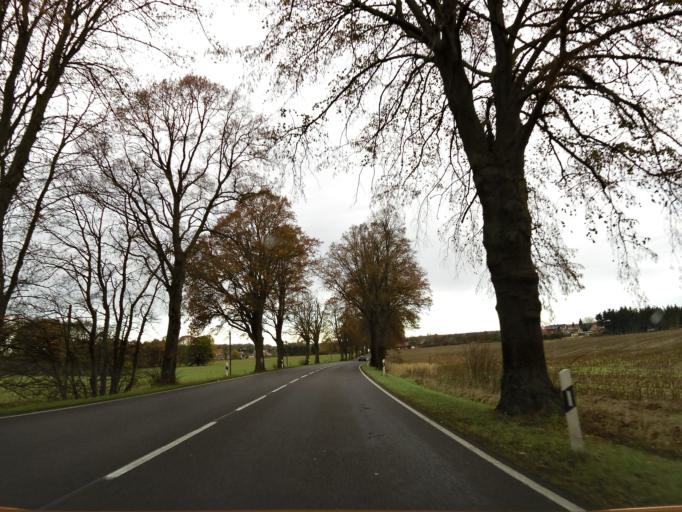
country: DE
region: Saxony-Anhalt
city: Letzlingen
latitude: 52.4348
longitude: 11.4816
